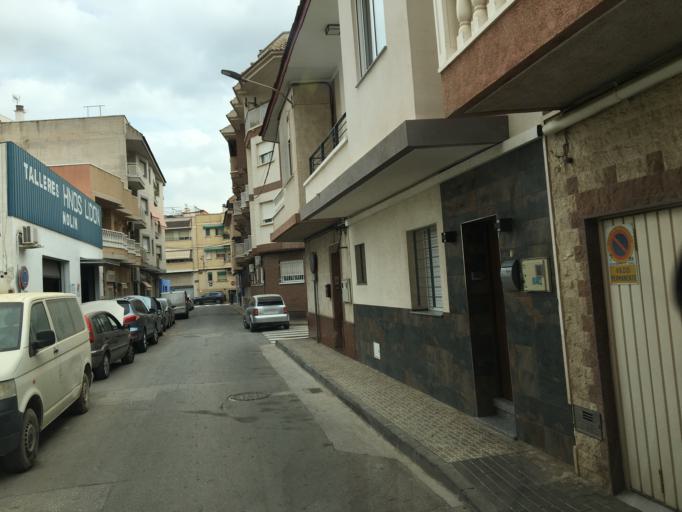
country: ES
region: Murcia
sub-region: Murcia
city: Beniel
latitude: 38.0443
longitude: -1.0029
